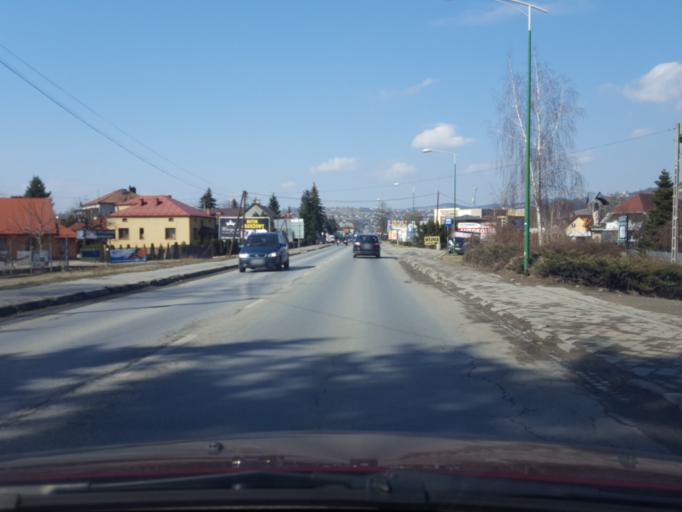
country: PL
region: Lesser Poland Voivodeship
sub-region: Powiat nowosadecki
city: Chelmiec
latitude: 49.6296
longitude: 20.6759
